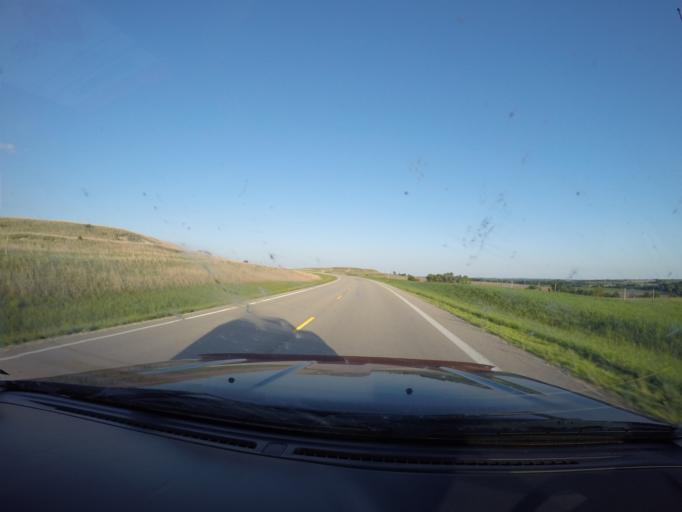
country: US
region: Kansas
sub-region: Marshall County
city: Blue Rapids
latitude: 39.6988
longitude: -96.8536
